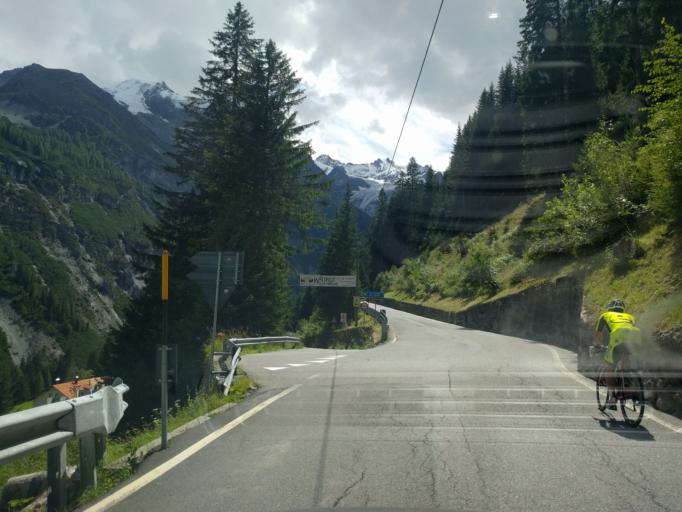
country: IT
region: Trentino-Alto Adige
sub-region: Bolzano
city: Stelvio
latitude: 46.5477
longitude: 10.5055
